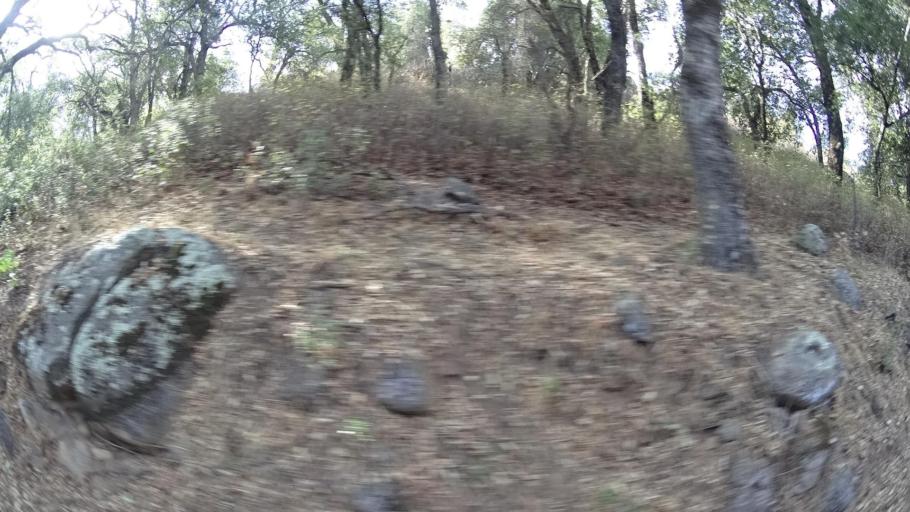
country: US
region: California
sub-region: San Diego County
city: Ramona
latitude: 33.1933
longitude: -116.7773
